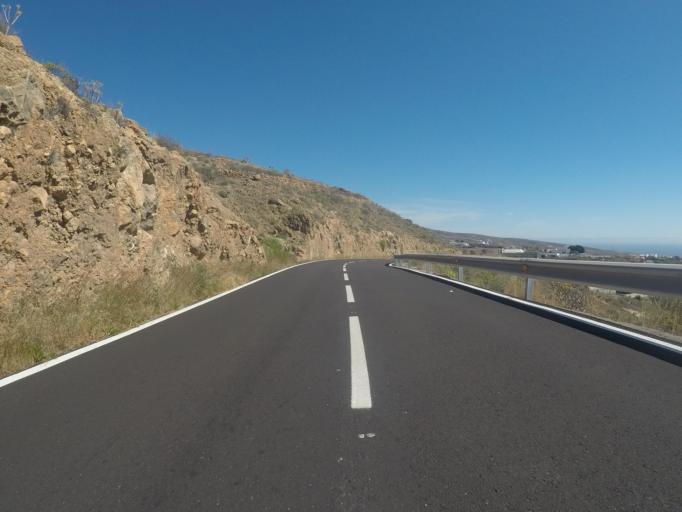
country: ES
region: Canary Islands
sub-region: Provincia de Santa Cruz de Tenerife
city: Lomo de Arico
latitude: 28.1766
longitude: -16.4876
